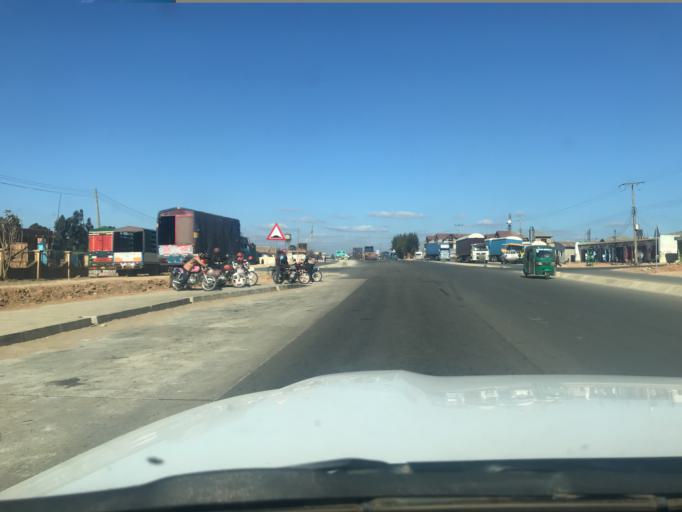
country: TZ
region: Njombe
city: Makumbako
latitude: -8.8424
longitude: 34.8185
